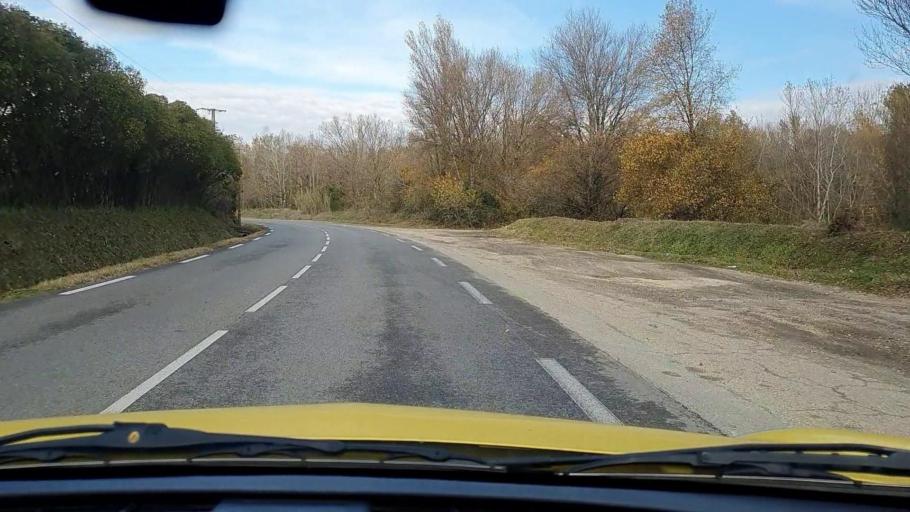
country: FR
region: Languedoc-Roussillon
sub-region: Departement du Gard
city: Comps
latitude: 43.8551
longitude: 4.5971
